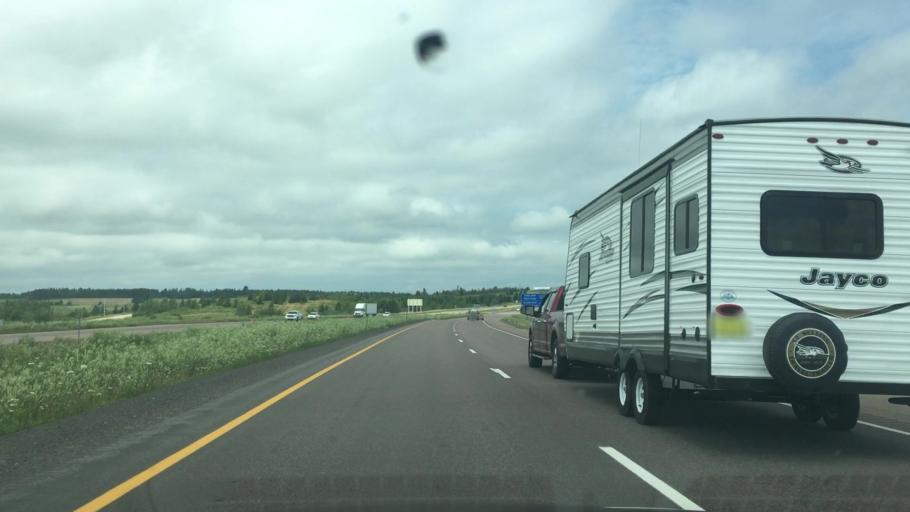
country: CA
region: Nova Scotia
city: Amherst
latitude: 45.8604
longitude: -64.2700
